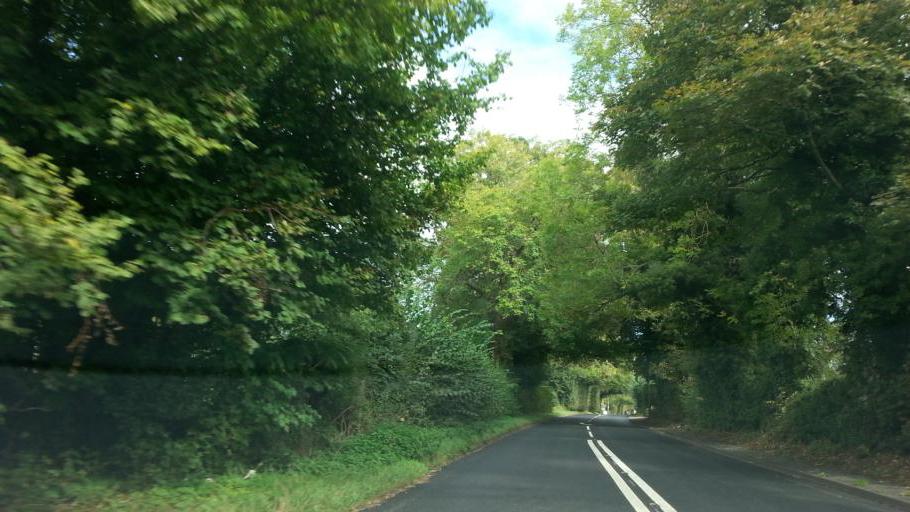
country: GB
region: England
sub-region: Gloucestershire
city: Painswick
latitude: 51.7804
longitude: -2.2046
